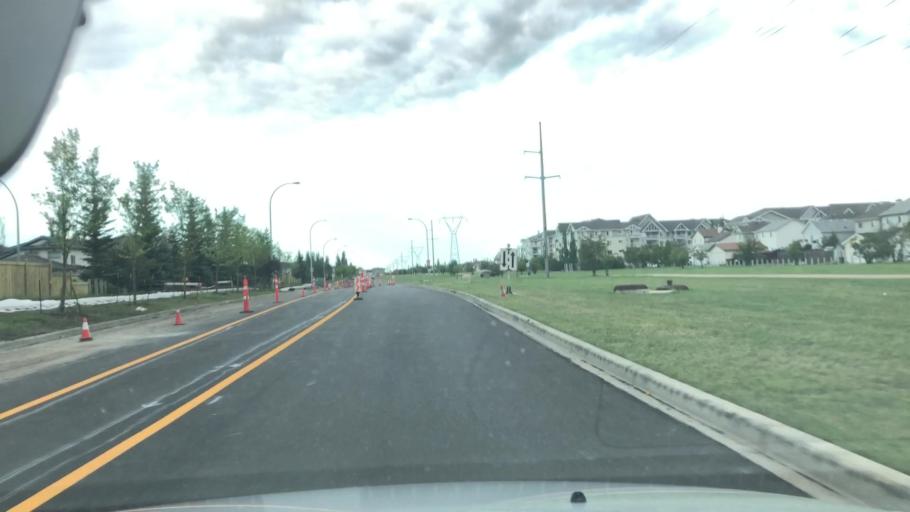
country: CA
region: Alberta
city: St. Albert
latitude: 53.6146
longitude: -113.5632
